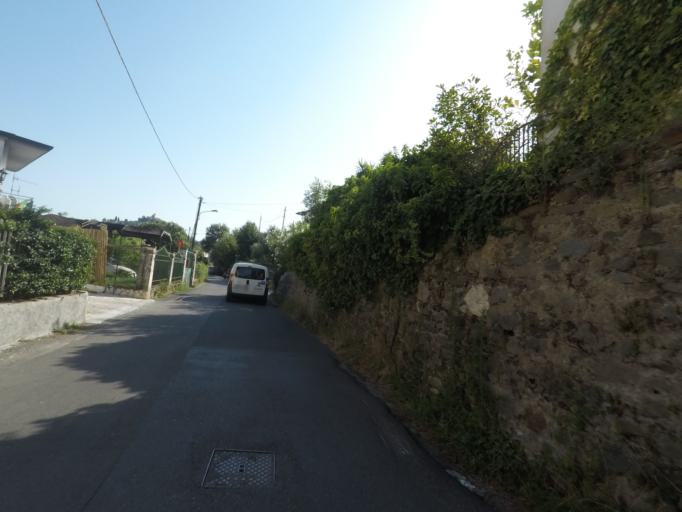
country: IT
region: Liguria
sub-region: Provincia di La Spezia
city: Casano-Dogana-Isola
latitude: 44.0881
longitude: 10.0448
